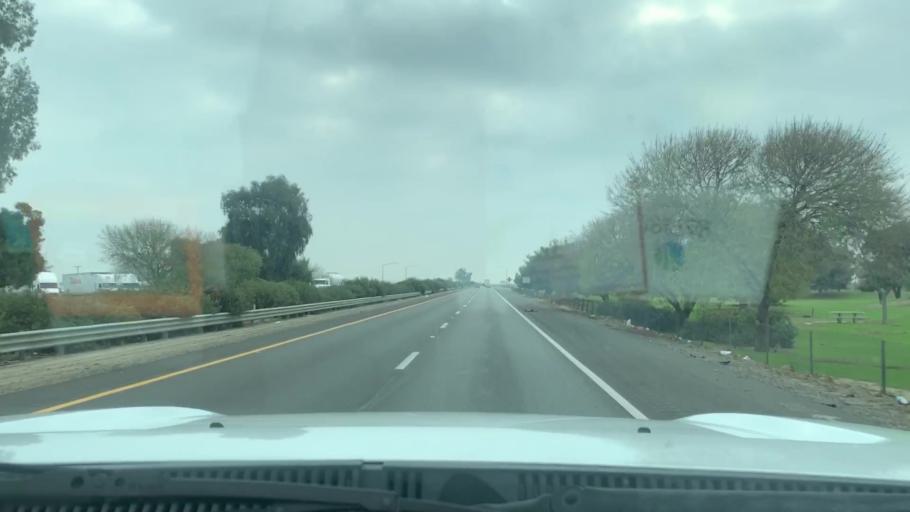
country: US
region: California
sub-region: Tulare County
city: Tipton
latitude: 36.1080
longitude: -119.3235
